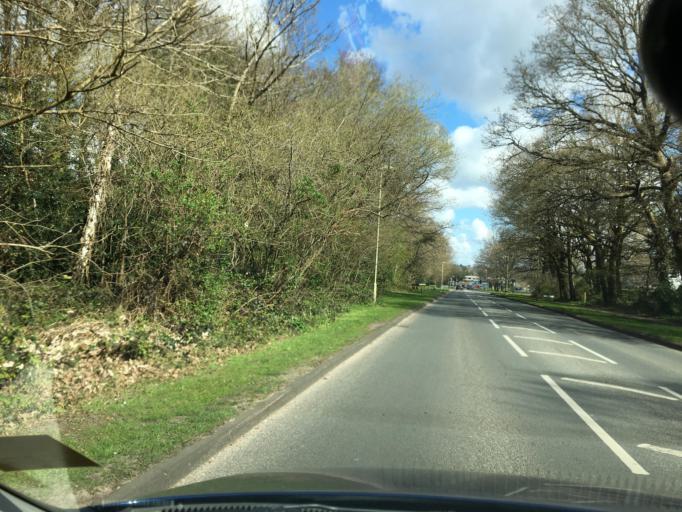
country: GB
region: England
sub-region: Hampshire
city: Yateley
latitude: 51.3400
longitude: -0.8314
